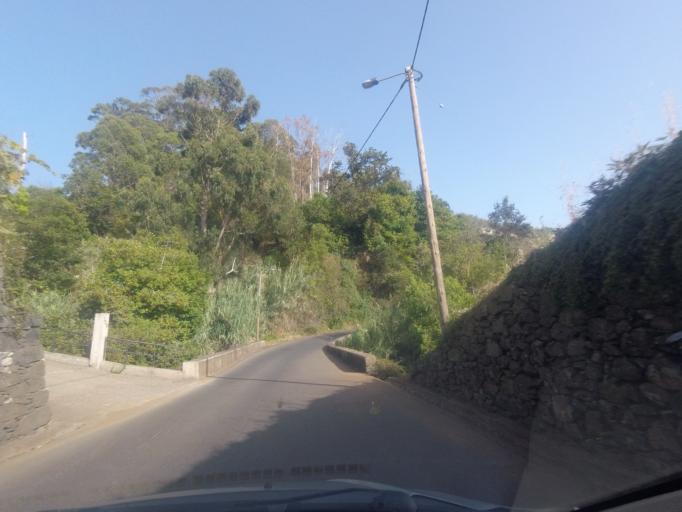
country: PT
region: Madeira
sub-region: Calheta
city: Arco da Calheta
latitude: 32.7073
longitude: -17.1256
